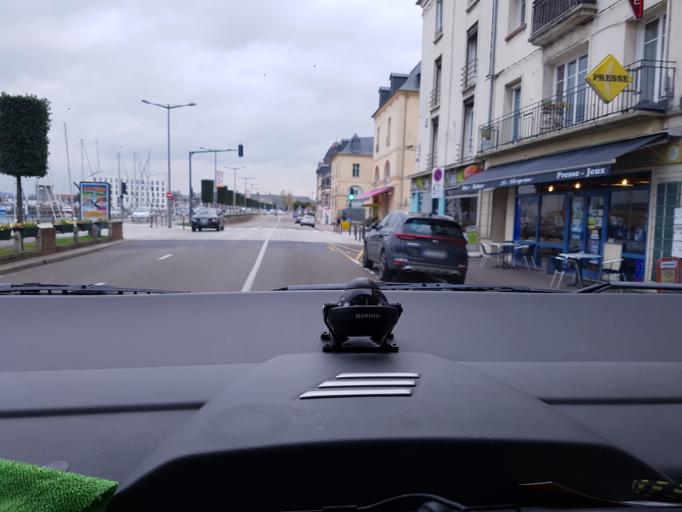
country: FR
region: Haute-Normandie
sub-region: Departement de la Seine-Maritime
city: Dieppe
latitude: 49.9252
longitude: 1.0802
